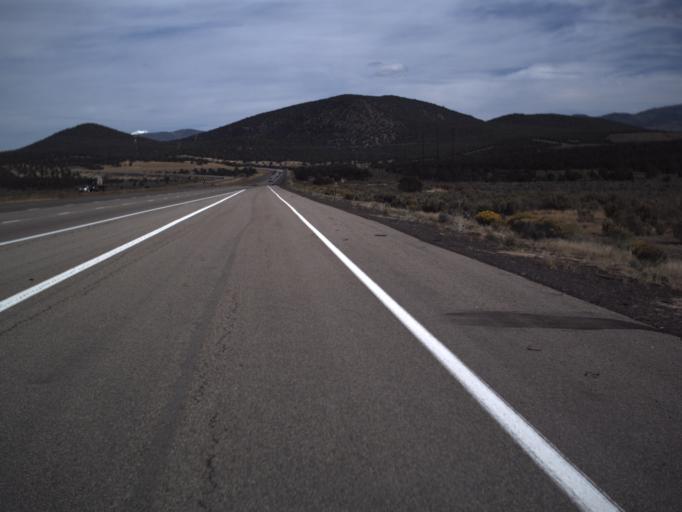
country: US
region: Utah
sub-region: Beaver County
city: Beaver
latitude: 38.1333
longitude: -112.6244
